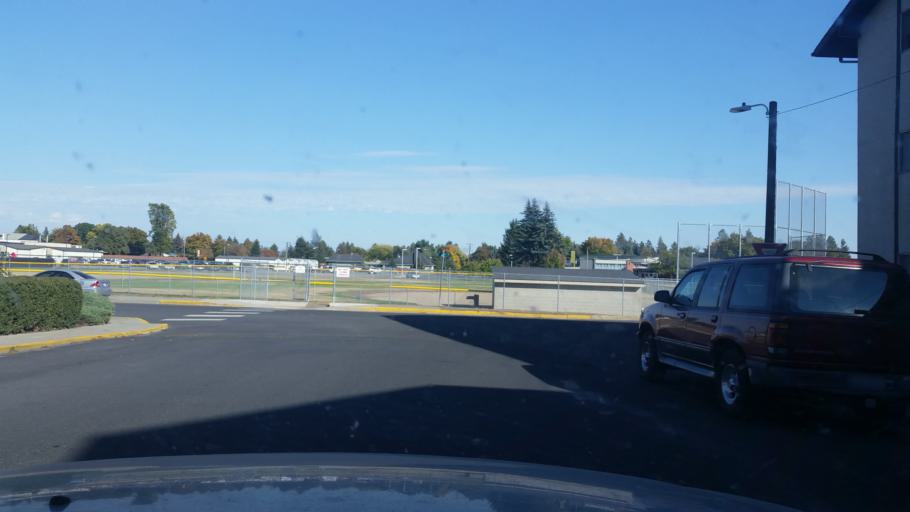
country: US
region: Washington
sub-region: Spokane County
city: Cheney
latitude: 47.4963
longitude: -117.5800
